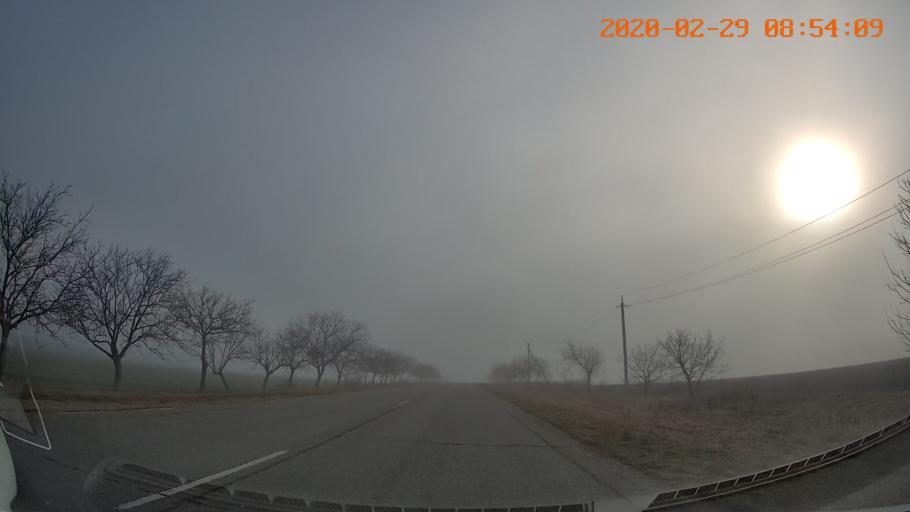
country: MD
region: Telenesti
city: Tiraspolul Nou
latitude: 46.9271
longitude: 29.5700
